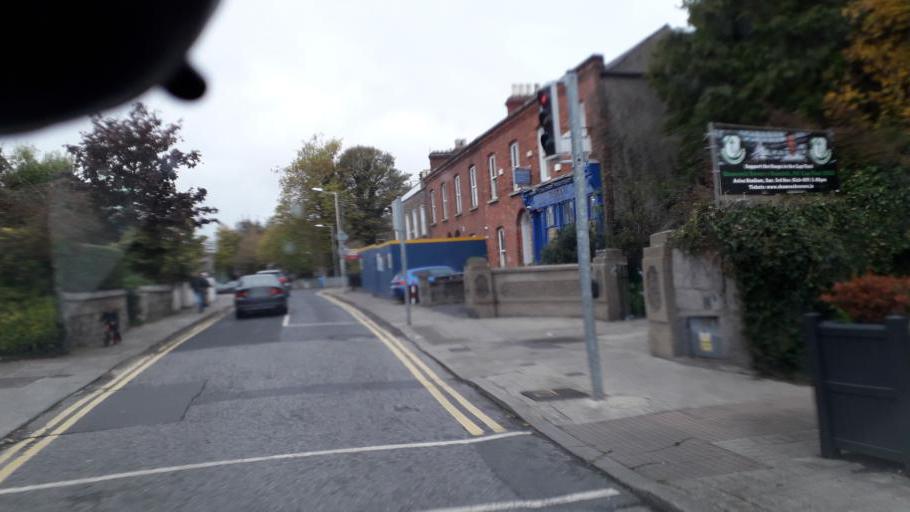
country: IE
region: Leinster
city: Rathmines
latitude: 53.3211
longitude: -6.2547
